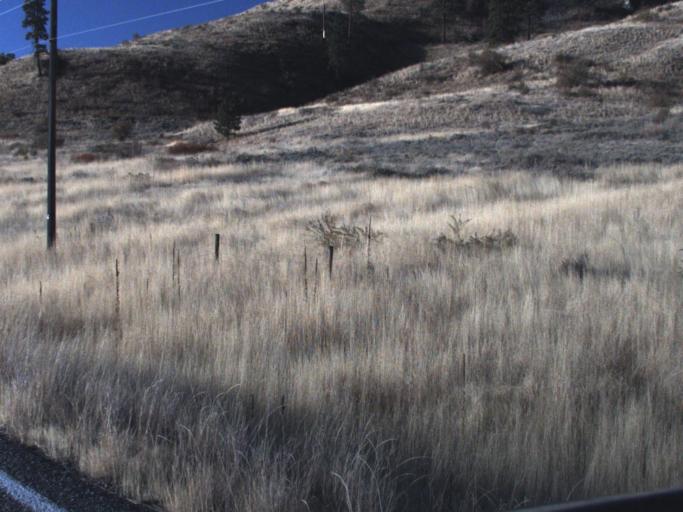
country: US
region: Washington
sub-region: Okanogan County
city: Coulee Dam
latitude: 47.9893
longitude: -118.6931
